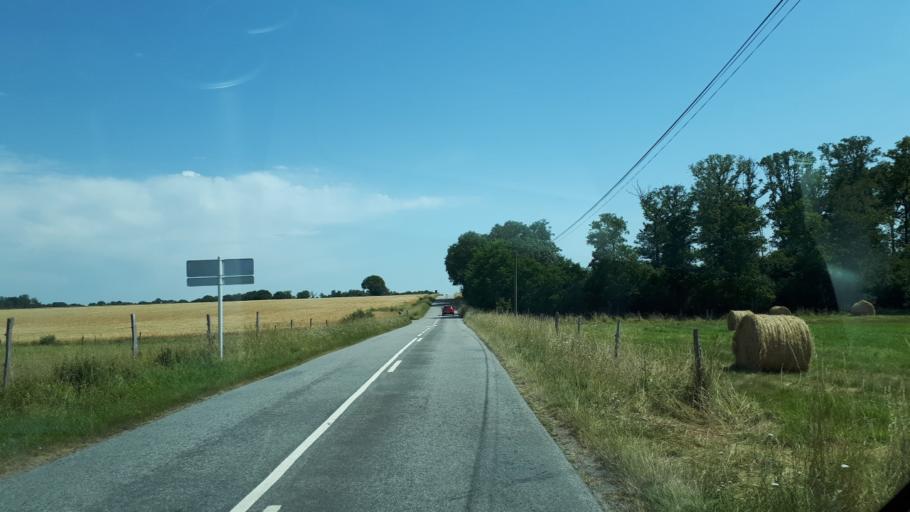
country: FR
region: Centre
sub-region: Departement d'Eure-et-Loir
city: Arrou
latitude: 48.0652
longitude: 1.1081
